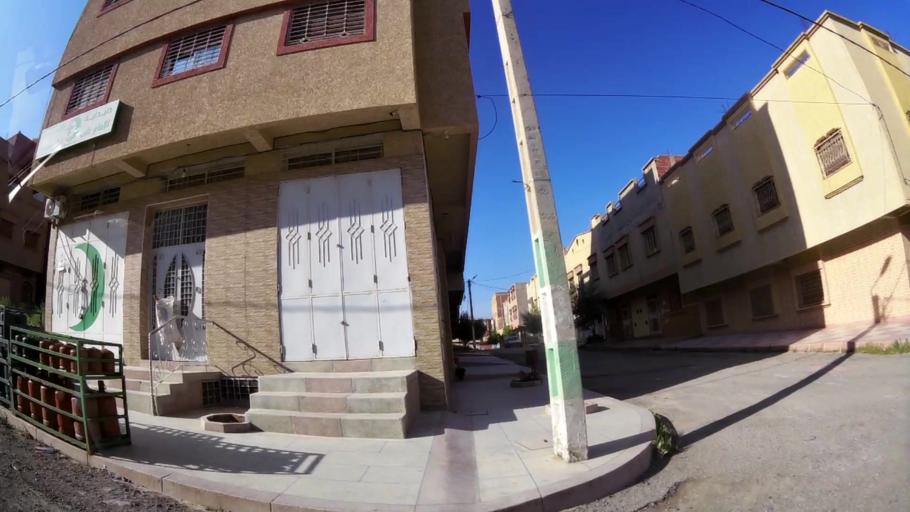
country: MA
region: Oriental
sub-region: Oujda-Angad
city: Oujda
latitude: 34.6764
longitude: -1.9424
